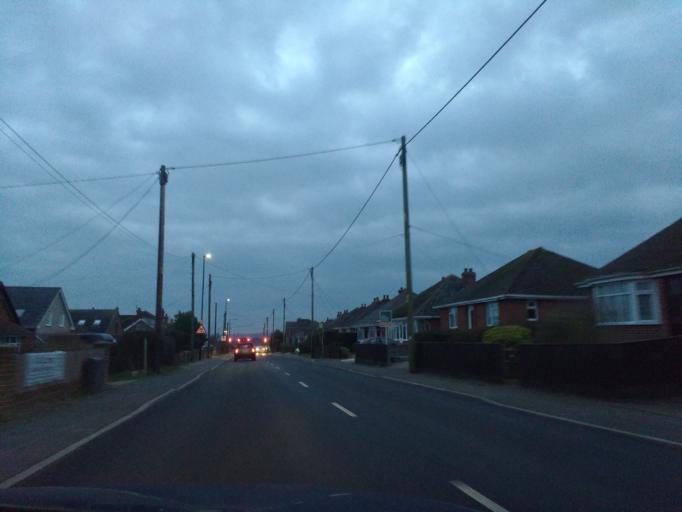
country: GB
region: England
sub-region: Isle of Wight
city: Northwood
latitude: 50.7248
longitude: -1.3049
